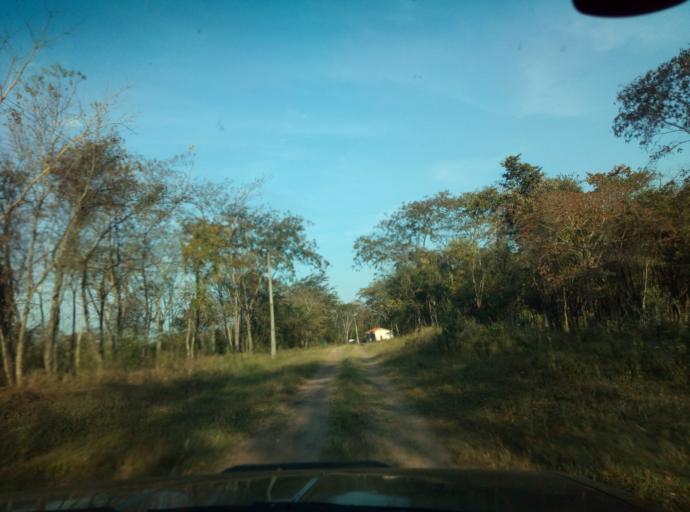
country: PY
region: Caaguazu
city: Doctor Cecilio Baez
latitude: -25.1994
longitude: -56.1360
